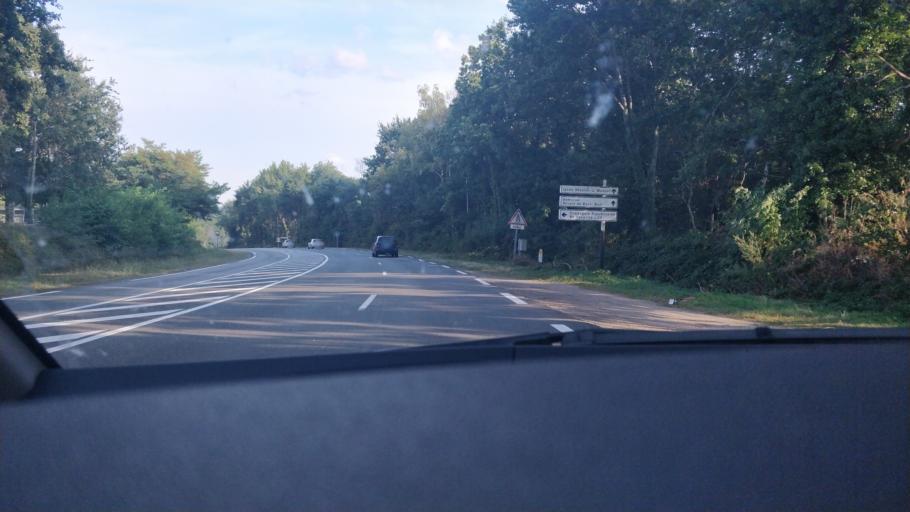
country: FR
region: Limousin
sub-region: Departement de la Haute-Vienne
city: Le Palais-sur-Vienne
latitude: 45.8572
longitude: 1.2904
